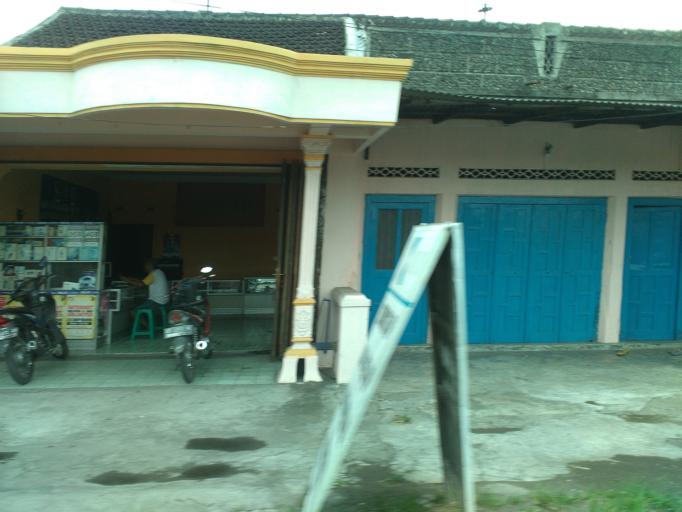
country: ID
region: Central Java
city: Ceper
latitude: -7.6605
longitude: 110.6735
